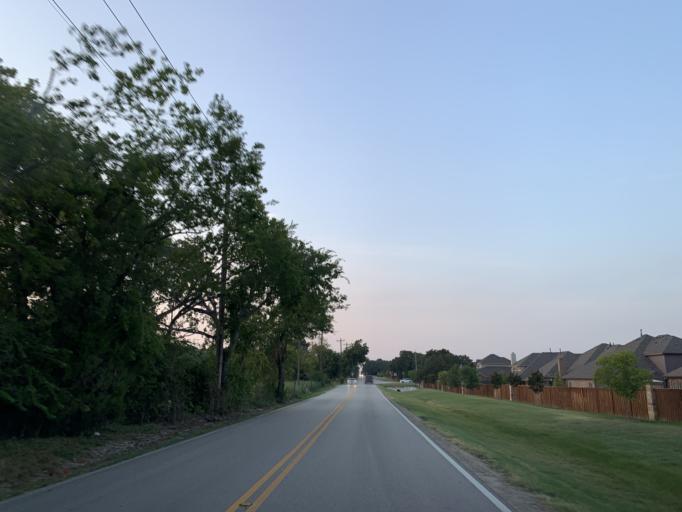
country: US
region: Texas
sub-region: Tarrant County
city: Keller
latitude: 32.9536
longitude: -97.2697
